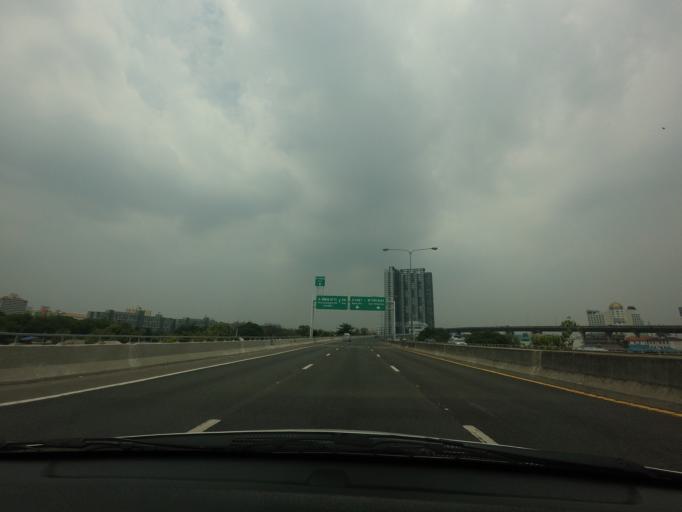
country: TH
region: Bangkok
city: Watthana
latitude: 13.7510
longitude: 100.6022
